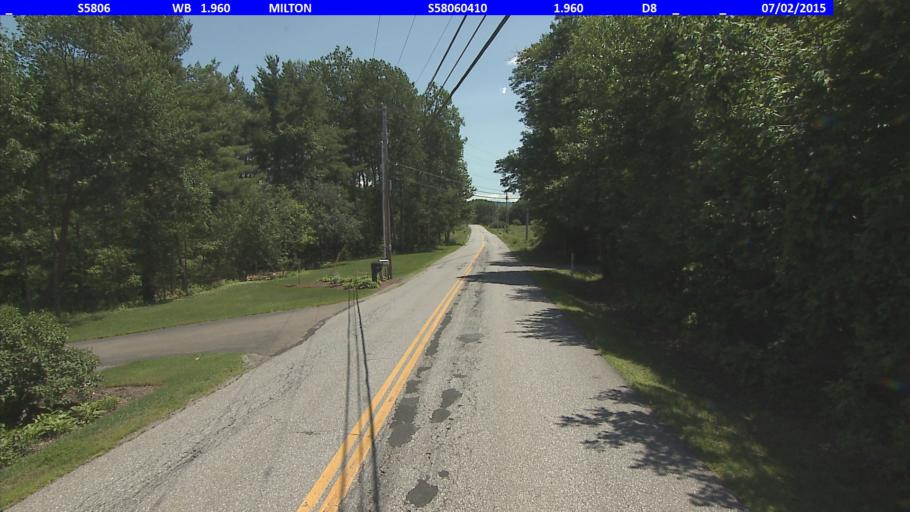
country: US
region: Vermont
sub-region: Chittenden County
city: Milton
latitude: 44.6615
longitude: -73.1489
